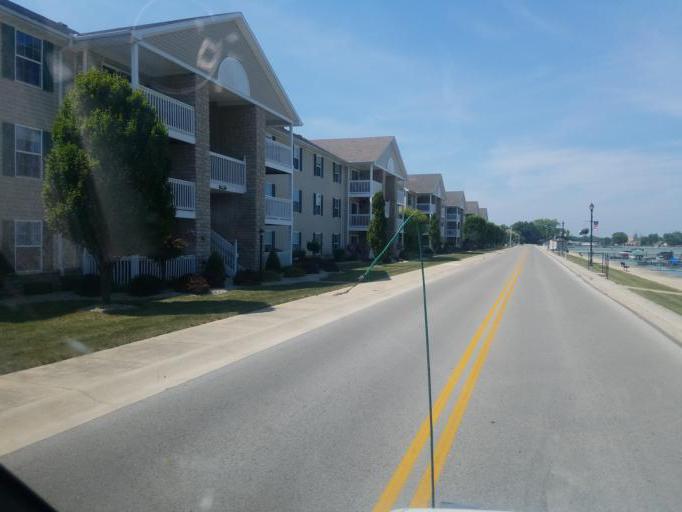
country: US
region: Ohio
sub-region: Mercer County
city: Celina
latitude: 40.5326
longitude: -84.5738
